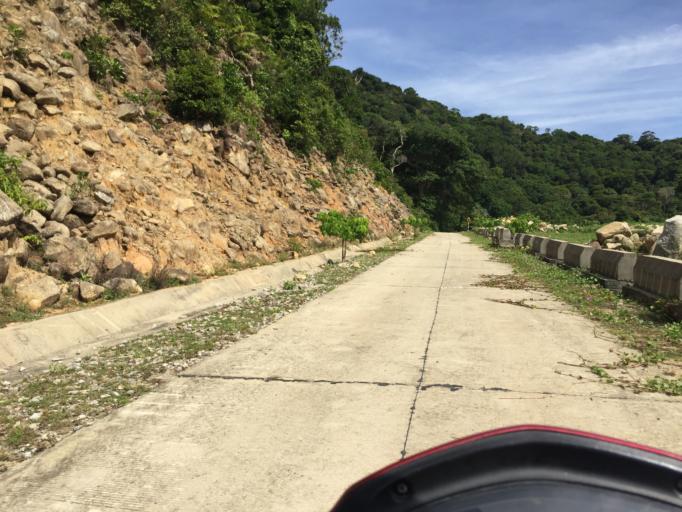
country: VN
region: Quang Nam
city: Hoi An
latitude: 15.9480
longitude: 108.5311
